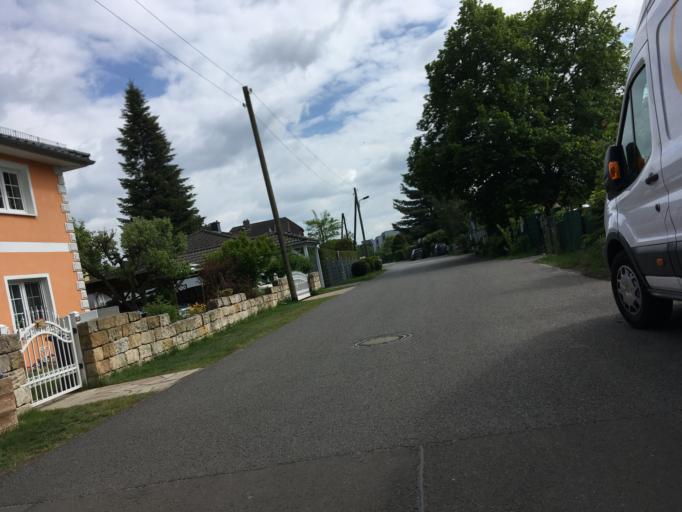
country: DE
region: Berlin
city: Grunau
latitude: 52.4273
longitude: 13.5681
